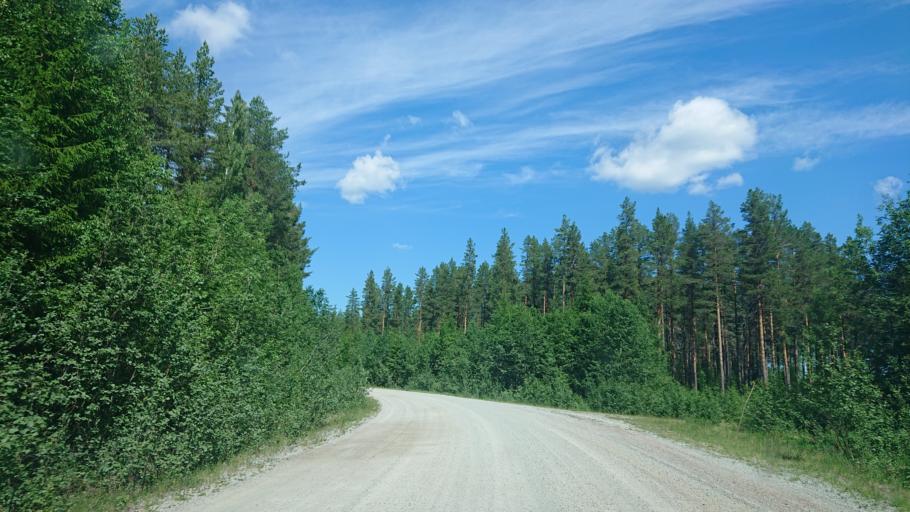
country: SE
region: Vaesternorrland
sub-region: Solleftea Kommun
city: Solleftea
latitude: 62.9609
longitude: 17.1525
